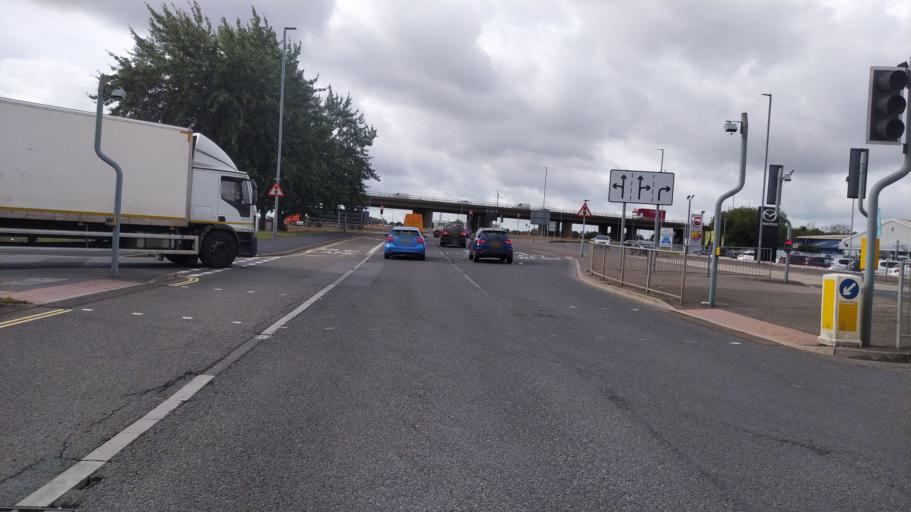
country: GB
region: England
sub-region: Portsmouth
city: Cosham
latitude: 50.8364
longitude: -1.0427
